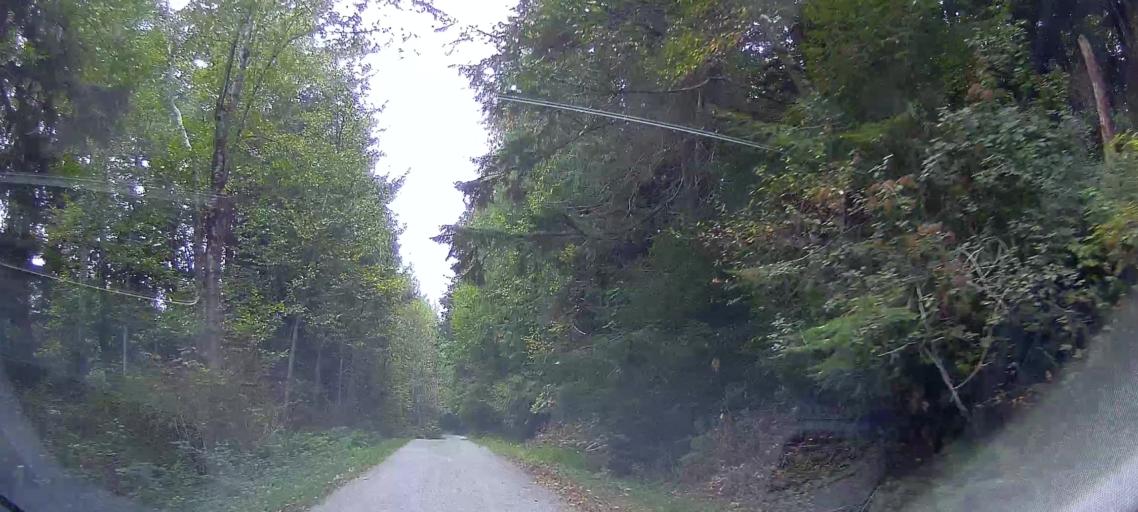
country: US
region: Washington
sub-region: Whatcom County
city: Geneva
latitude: 48.6129
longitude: -122.4351
